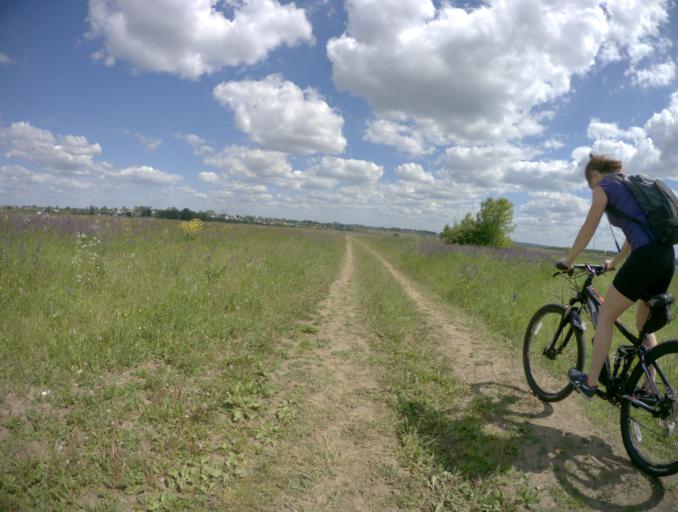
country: RU
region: Vladimir
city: Bogolyubovo
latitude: 56.1827
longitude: 40.4839
